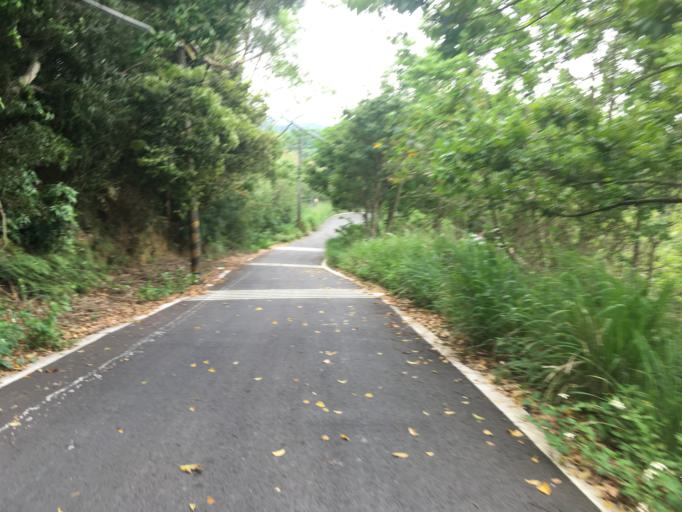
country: TW
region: Taiwan
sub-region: Hsinchu
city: Hsinchu
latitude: 24.7401
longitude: 120.9828
